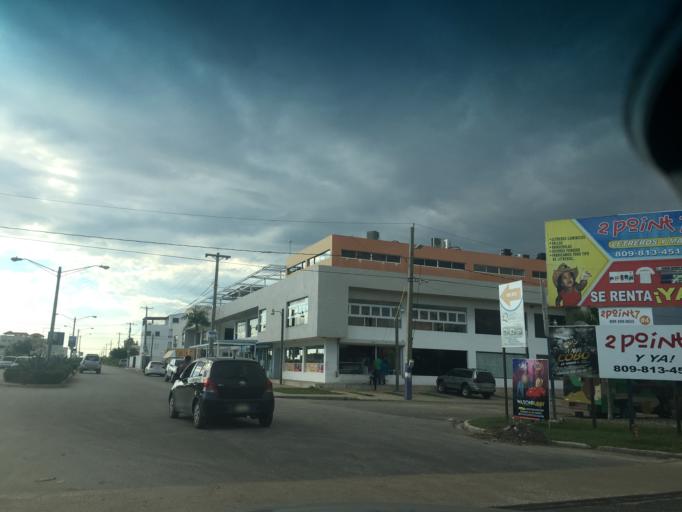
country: DO
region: La Romana
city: La Romana
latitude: 18.4237
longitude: -68.9915
